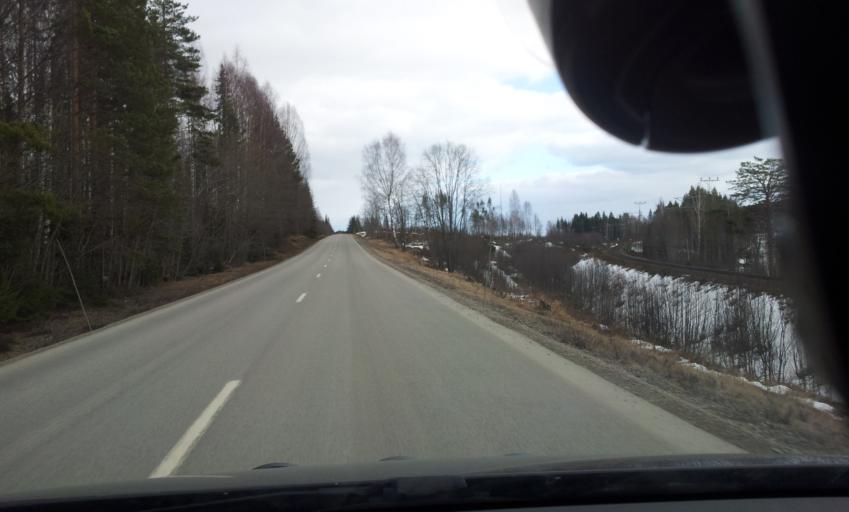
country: SE
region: Gaevleborg
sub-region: Ljusdals Kommun
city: Farila
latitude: 62.1301
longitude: 15.7024
